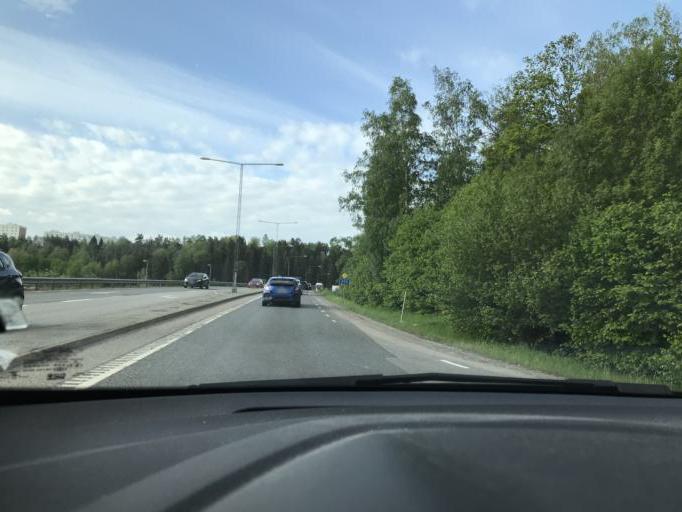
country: SE
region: Stockholm
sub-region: Botkyrka Kommun
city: Tumba
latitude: 59.2012
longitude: 17.8417
